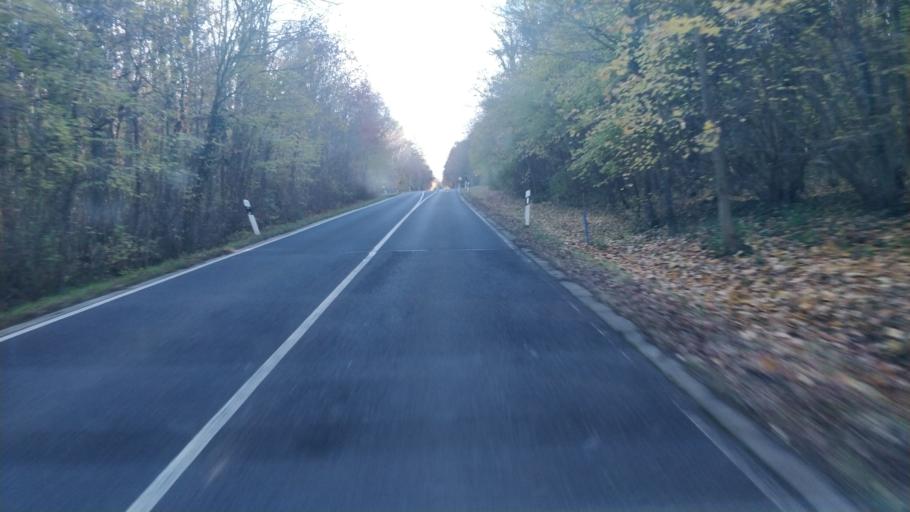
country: DE
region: North Rhine-Westphalia
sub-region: Regierungsbezirk Koln
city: Rheinbach
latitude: 50.6185
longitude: 6.8913
